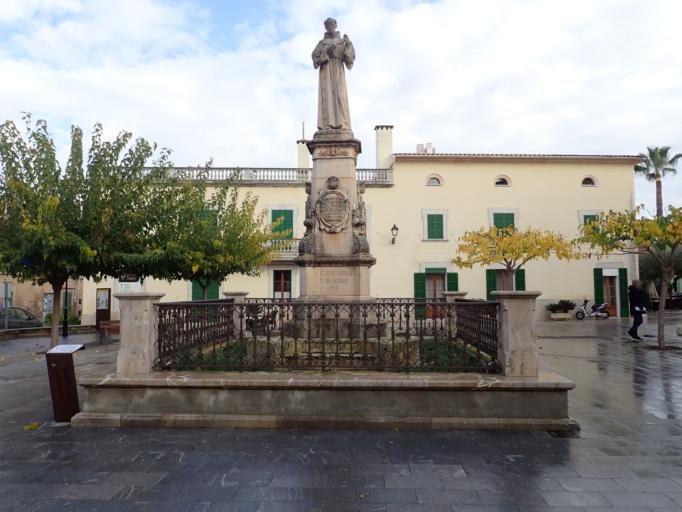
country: ES
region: Balearic Islands
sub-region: Illes Balears
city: Petra
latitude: 39.6144
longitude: 3.1120
